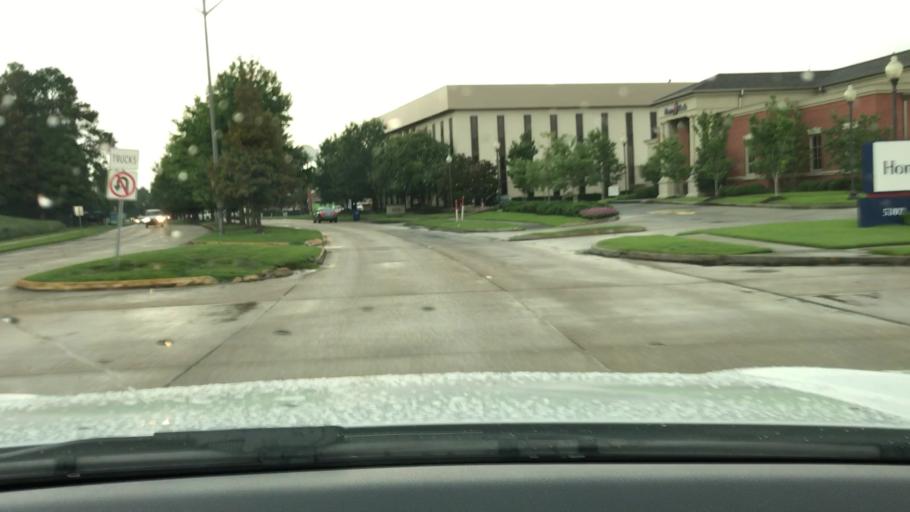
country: US
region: Louisiana
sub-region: East Baton Rouge Parish
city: Baton Rouge
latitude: 30.4249
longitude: -91.1353
